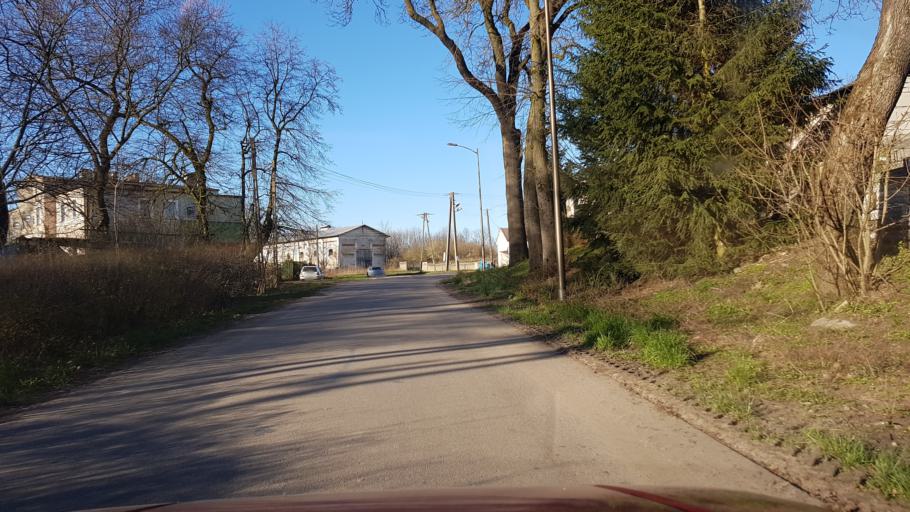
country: PL
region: West Pomeranian Voivodeship
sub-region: Powiat stargardzki
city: Stara Dabrowa
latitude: 53.3768
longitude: 15.1083
